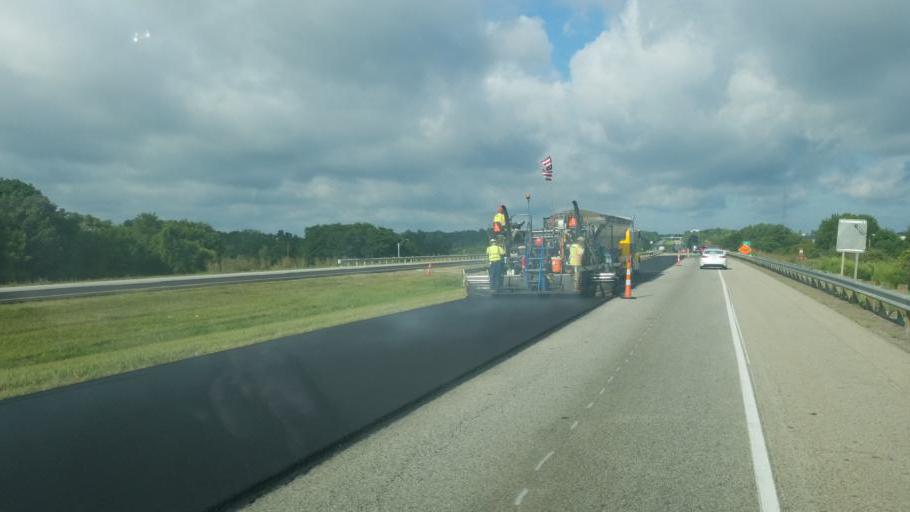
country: US
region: Ohio
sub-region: Stark County
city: Genoa
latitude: 40.7788
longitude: -81.4259
